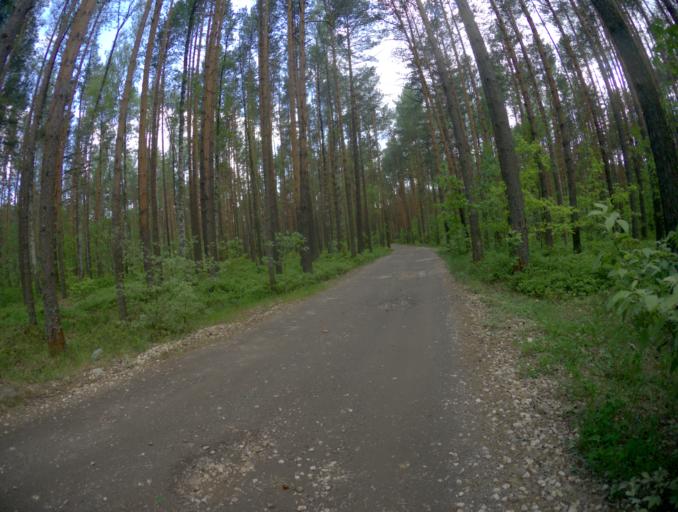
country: RU
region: Vladimir
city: Kommunar
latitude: 56.1003
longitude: 40.4570
